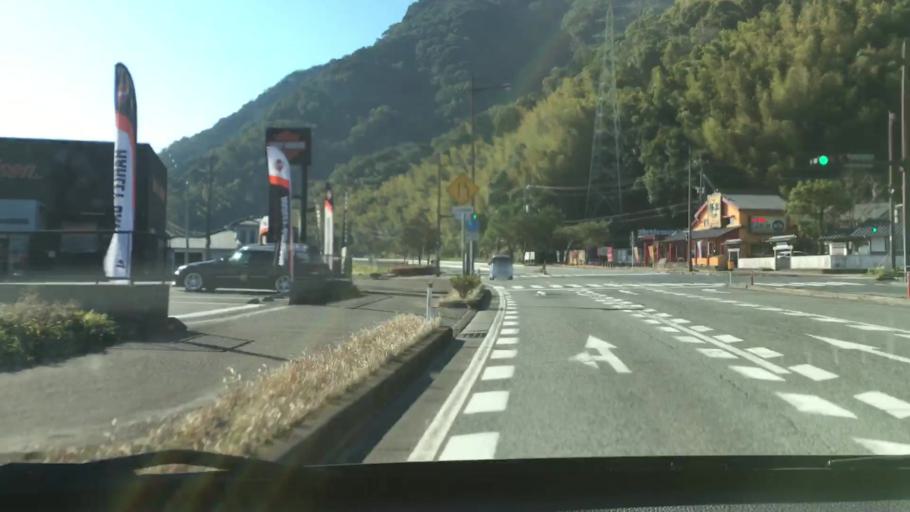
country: JP
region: Kagoshima
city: Kajiki
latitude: 31.7036
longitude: 130.6118
